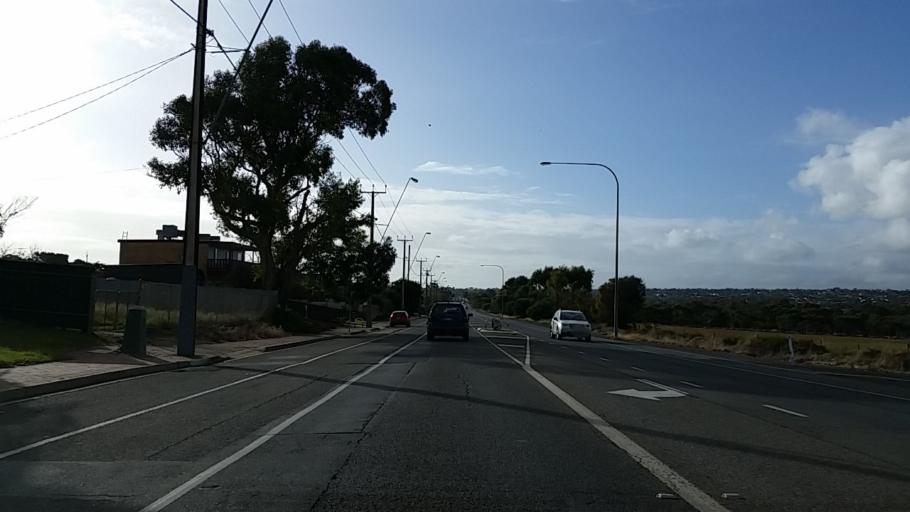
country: AU
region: South Australia
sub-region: Adelaide
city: Port Noarlunga
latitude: -35.1650
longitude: 138.4755
